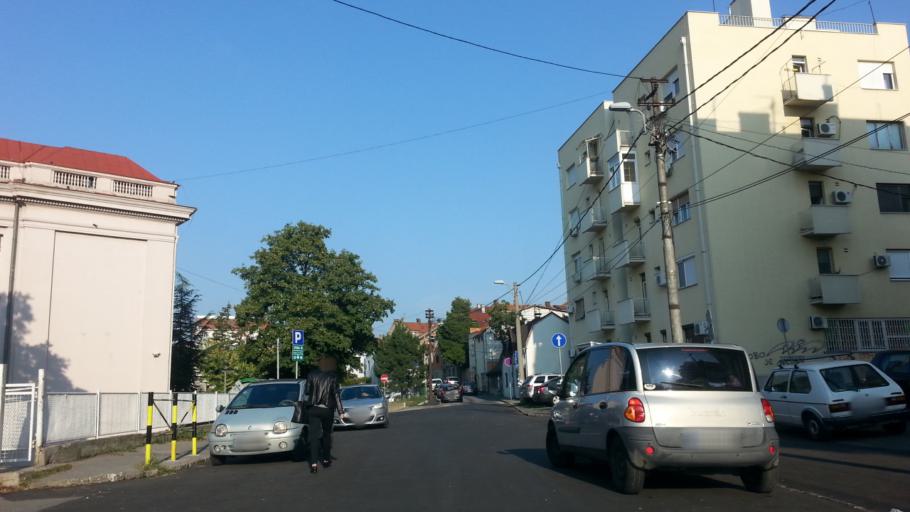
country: RS
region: Central Serbia
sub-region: Belgrade
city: Vracar
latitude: 44.7948
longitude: 20.4815
